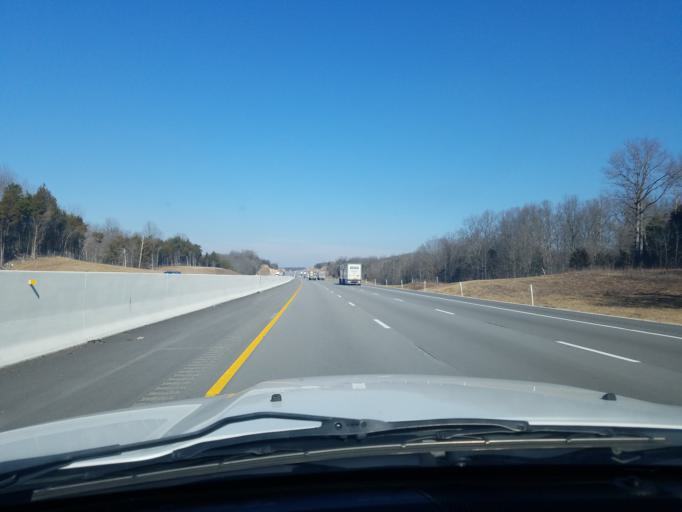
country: US
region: Kentucky
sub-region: Hart County
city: Munfordville
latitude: 37.4111
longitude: -85.8814
